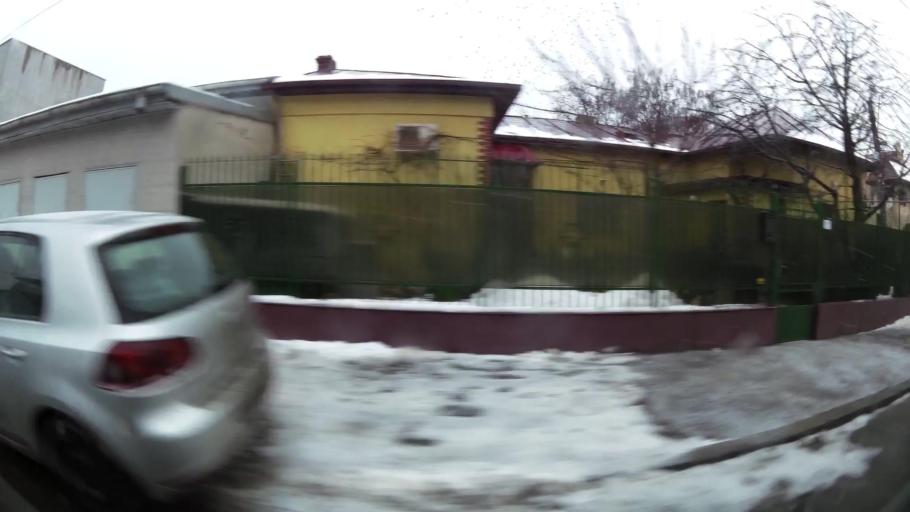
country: RO
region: Ilfov
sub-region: Comuna Chiajna
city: Rosu
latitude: 44.4695
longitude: 26.0481
